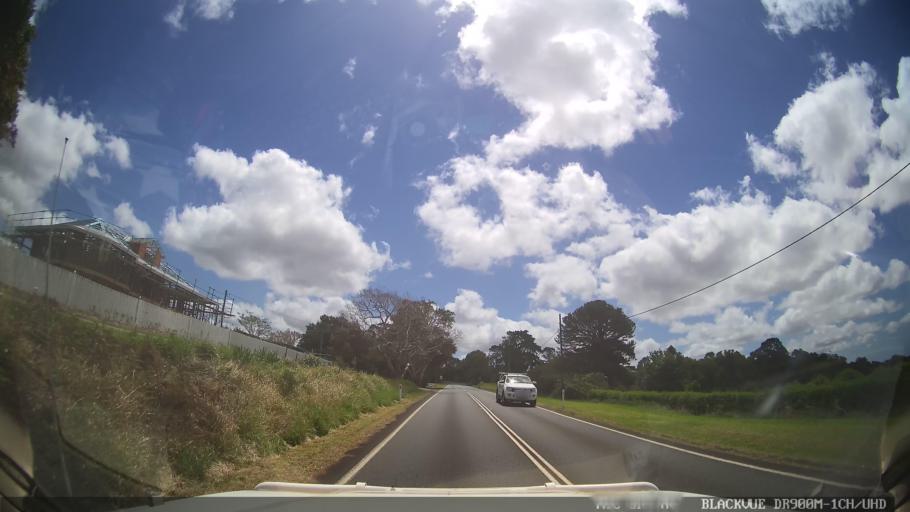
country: AU
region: Queensland
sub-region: Sunshine Coast
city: Nambour
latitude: -26.6672
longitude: 152.8807
